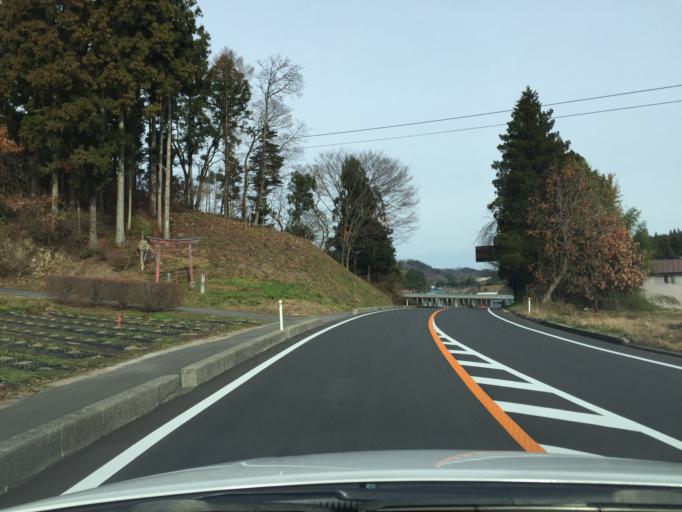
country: JP
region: Fukushima
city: Funehikimachi-funehiki
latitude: 37.3589
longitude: 140.6050
